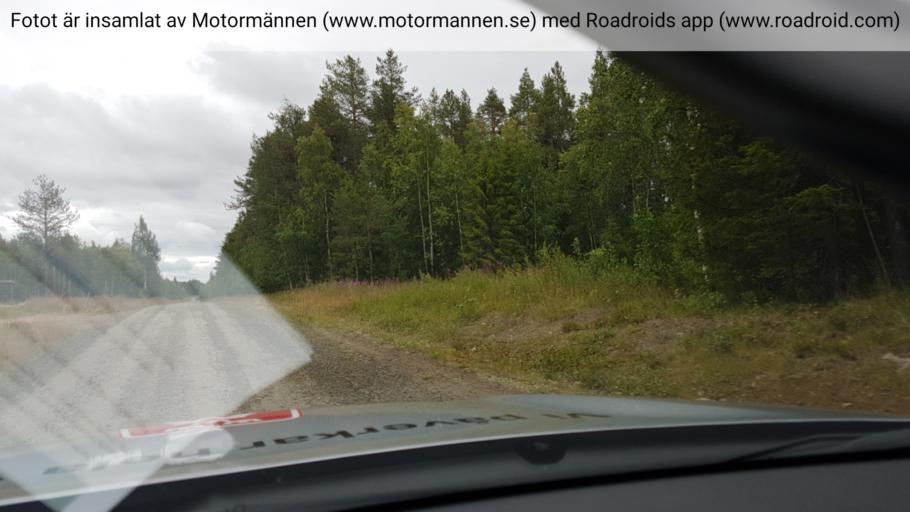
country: SE
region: Norrbotten
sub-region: Pajala Kommun
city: Pajala
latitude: 66.9788
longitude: 22.8906
